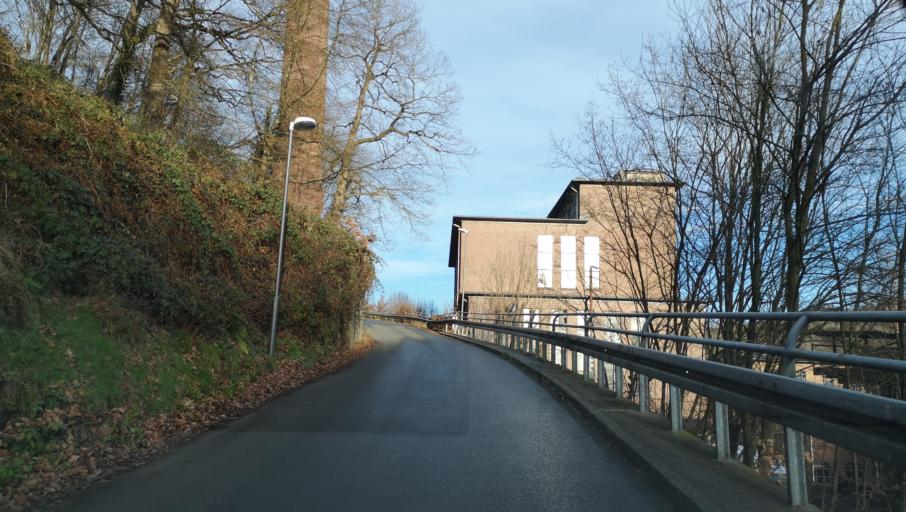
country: DE
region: North Rhine-Westphalia
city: Radevormwald
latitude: 51.2213
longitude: 7.3159
